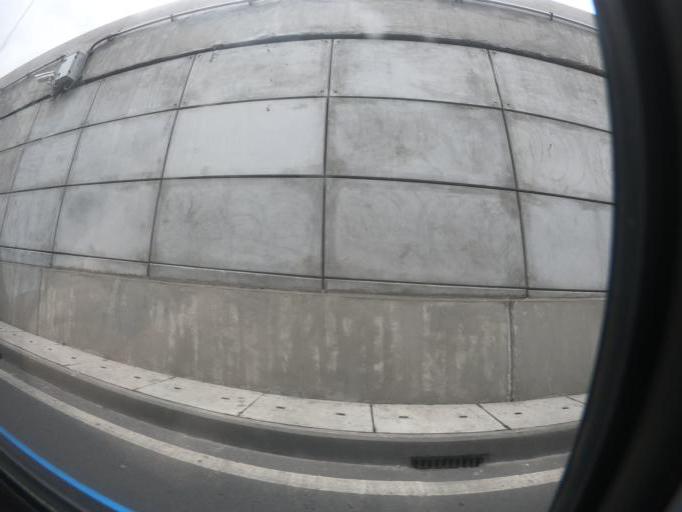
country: TH
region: Bangkok
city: Suan Luang
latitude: 13.7377
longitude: 100.6217
